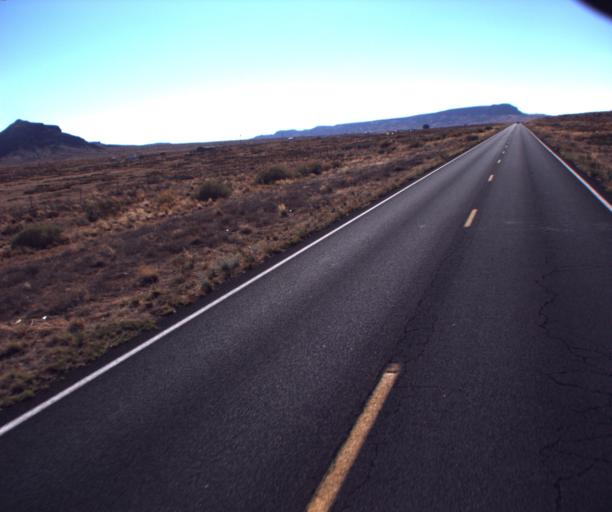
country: US
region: Arizona
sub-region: Navajo County
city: Dilkon
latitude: 35.4821
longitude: -110.4279
